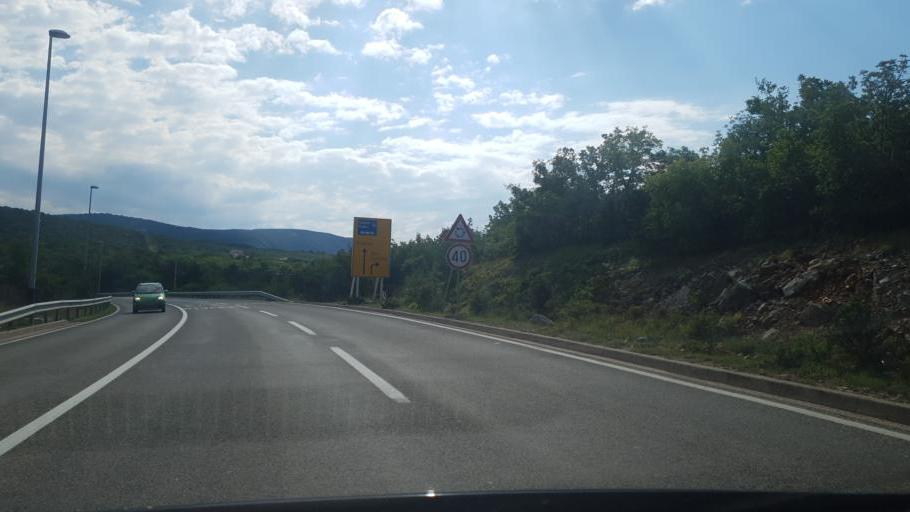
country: HR
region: Primorsko-Goranska
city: Kraljevica
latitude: 45.2592
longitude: 14.5880
